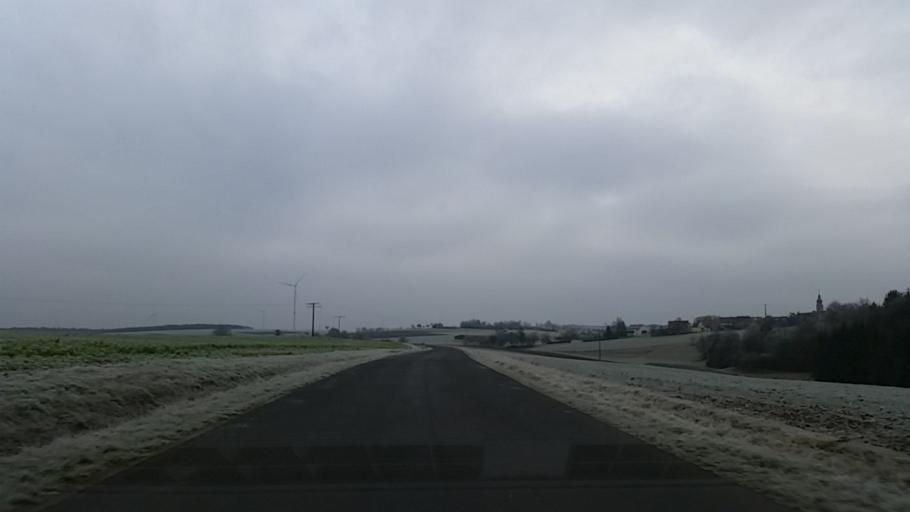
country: DE
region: Bavaria
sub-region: Regierungsbezirk Unterfranken
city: Fuchsstadt
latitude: 50.0463
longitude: 9.9160
